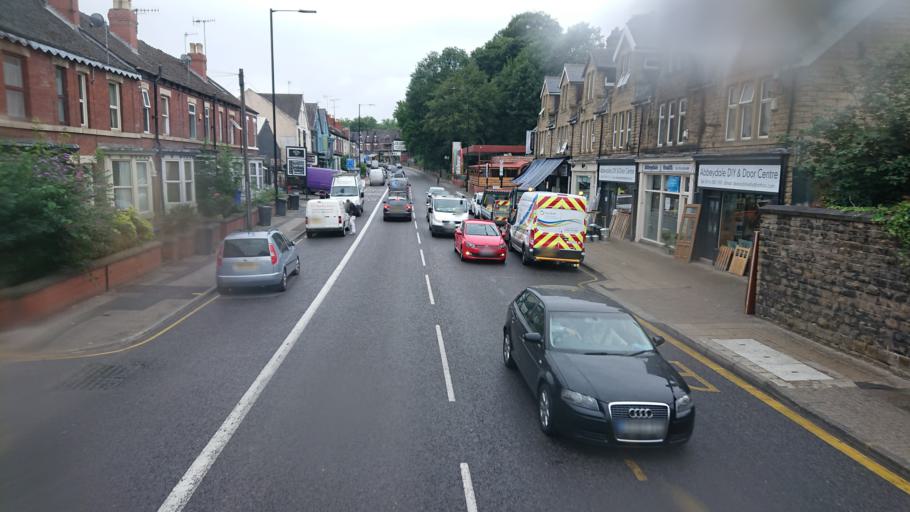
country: GB
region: England
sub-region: Sheffield
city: Sheffield
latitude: 53.3568
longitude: -1.4839
